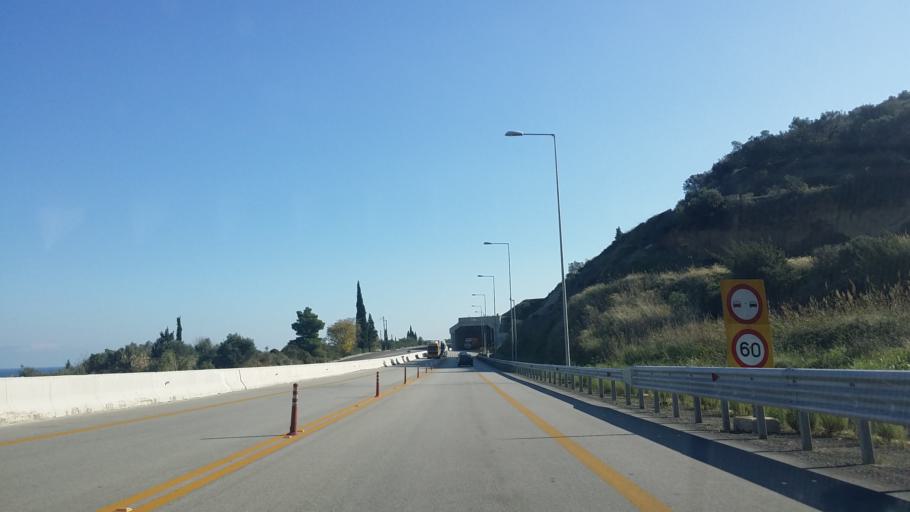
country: GR
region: West Greece
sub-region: Nomos Achaias
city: Temeni
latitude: 38.2090
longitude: 22.1318
